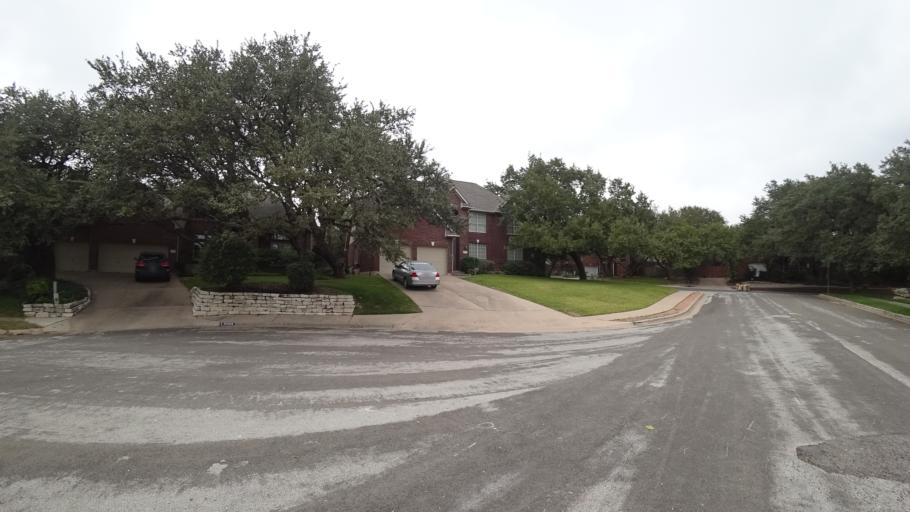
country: US
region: Texas
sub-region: Williamson County
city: Anderson Mill
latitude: 30.4347
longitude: -97.8226
